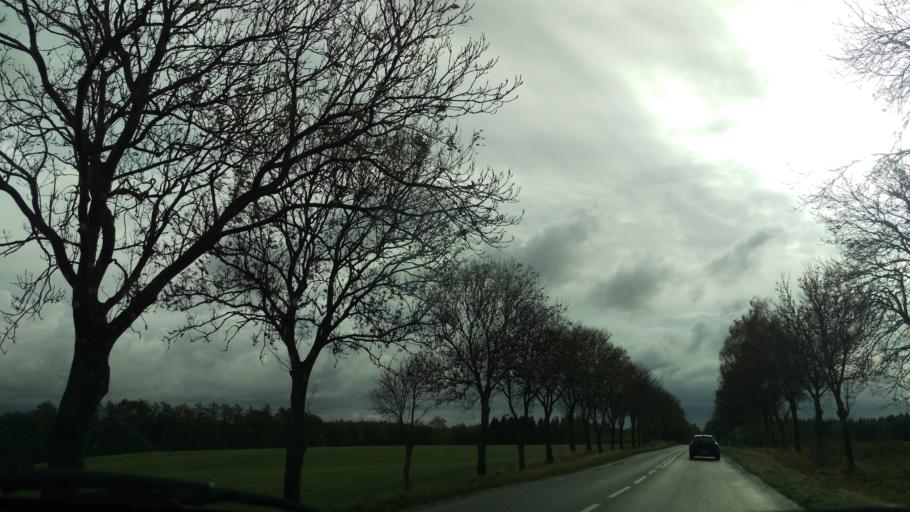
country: PL
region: West Pomeranian Voivodeship
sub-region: Powiat gryficki
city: Gryfice
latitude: 53.8654
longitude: 15.2196
